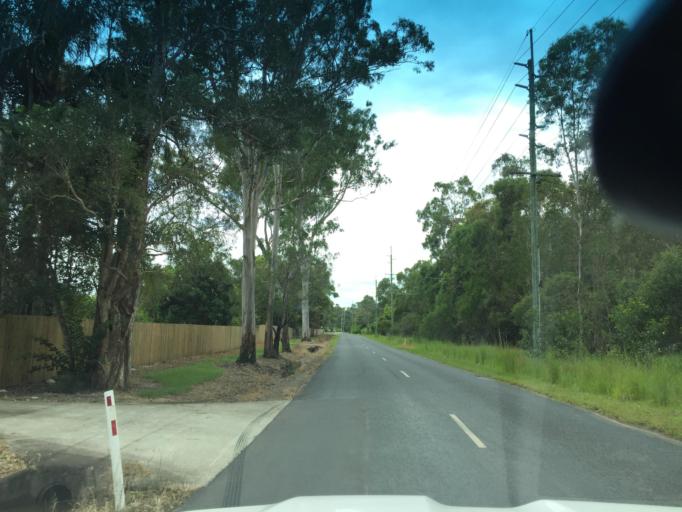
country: AU
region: Queensland
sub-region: Moreton Bay
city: Burpengary
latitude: -27.1716
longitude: 152.9845
